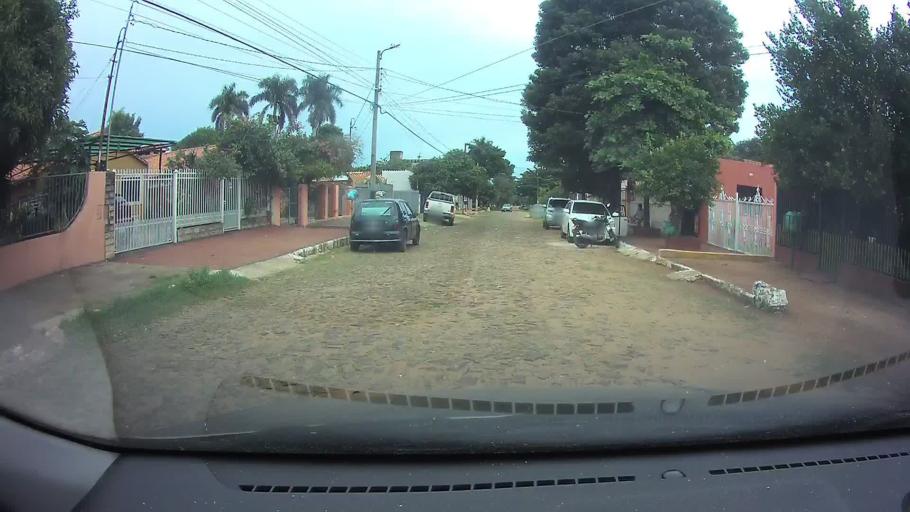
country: PY
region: Central
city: Limpio
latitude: -25.2352
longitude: -57.4768
